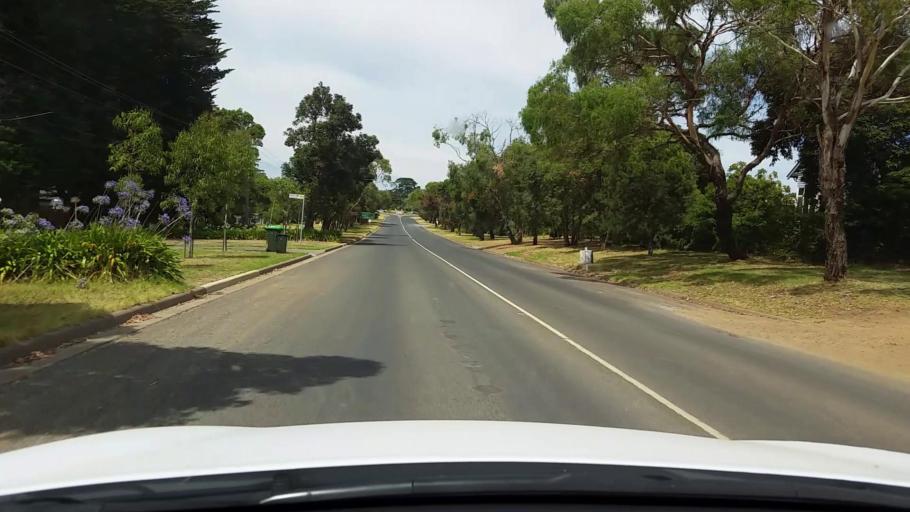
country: AU
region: Victoria
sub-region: Mornington Peninsula
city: Merricks
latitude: -38.4710
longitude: 145.0196
